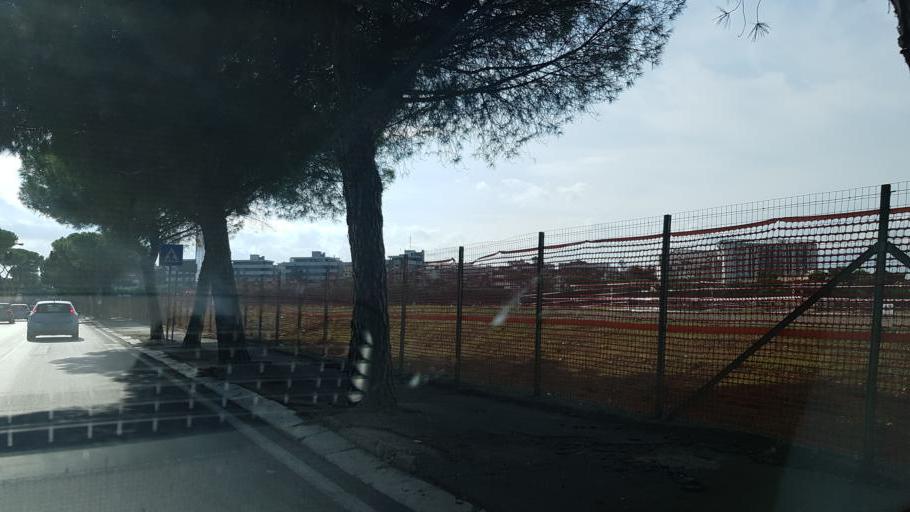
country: IT
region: Apulia
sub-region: Provincia di Foggia
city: Foggia
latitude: 41.4583
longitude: 15.5643
